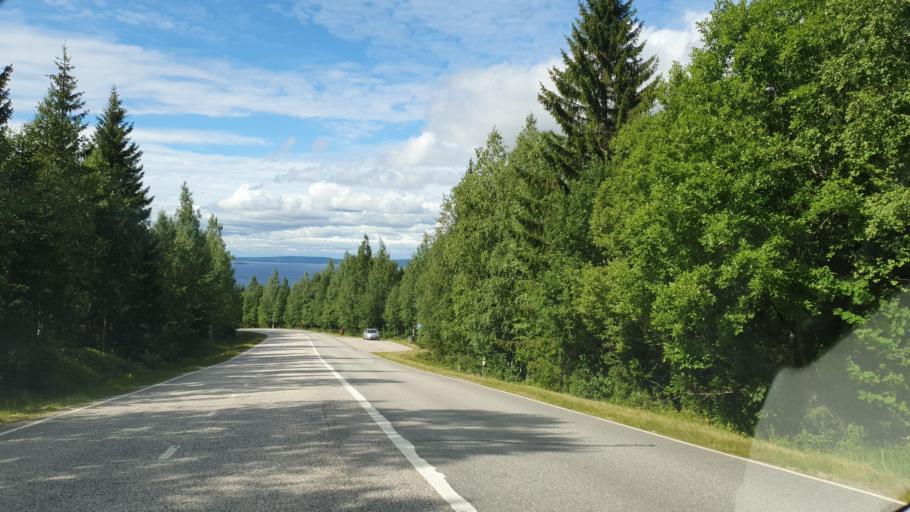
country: FI
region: Kainuu
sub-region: Kajaani
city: Vuokatti
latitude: 64.1299
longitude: 28.2532
